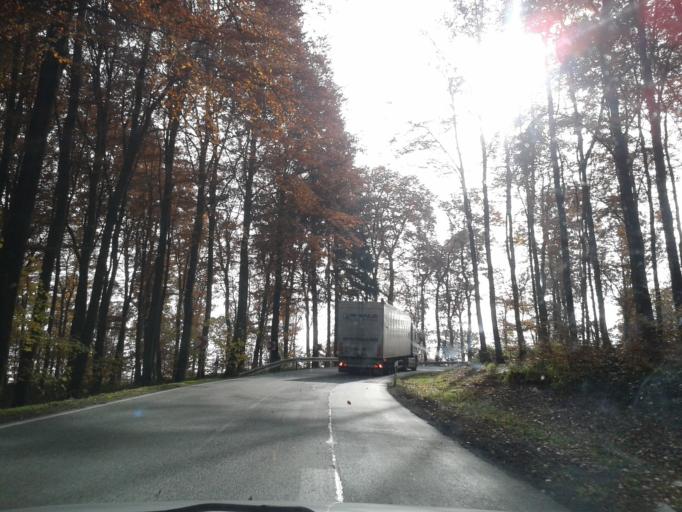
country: DE
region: North Rhine-Westphalia
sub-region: Regierungsbezirk Arnsberg
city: Bestwig
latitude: 51.4022
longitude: 8.4207
